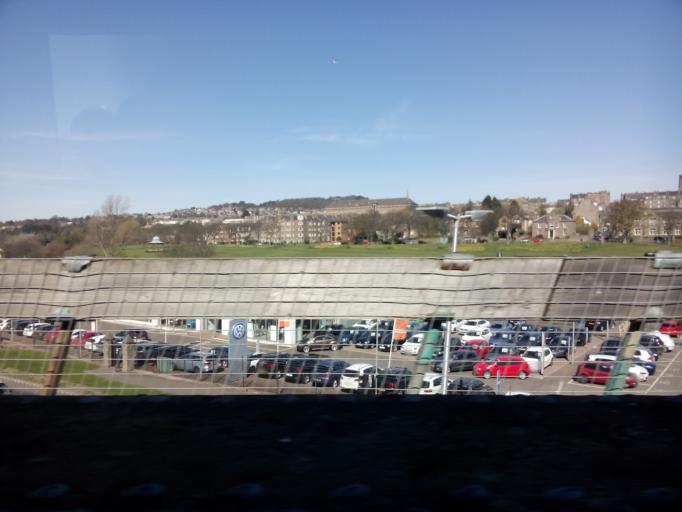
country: GB
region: Scotland
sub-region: Dundee City
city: Dundee
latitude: 56.4513
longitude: -2.9906
